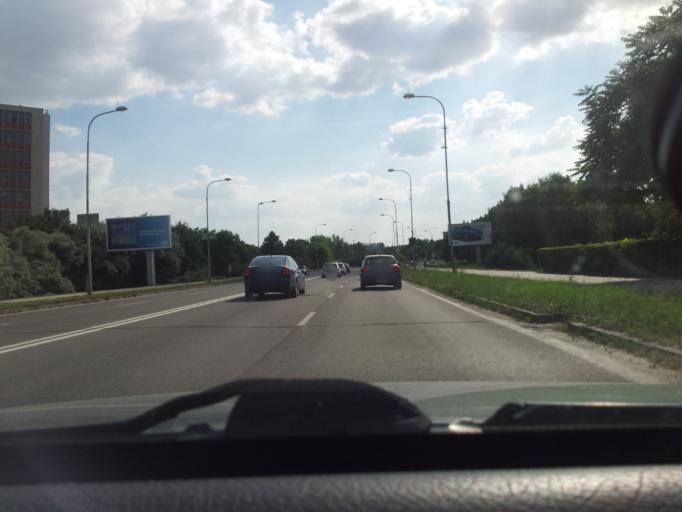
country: SK
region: Nitriansky
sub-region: Okres Nitra
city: Nitra
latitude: 48.3086
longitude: 18.0942
